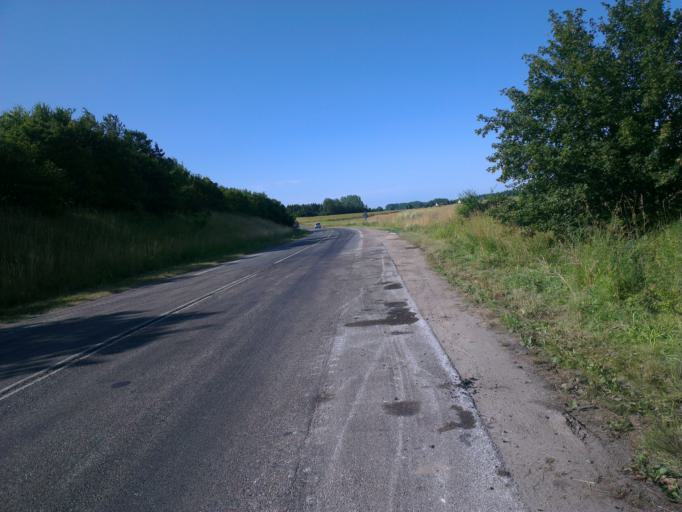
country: DK
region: Capital Region
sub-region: Frederikssund Kommune
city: Jaegerspris
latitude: 55.8284
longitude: 12.0147
